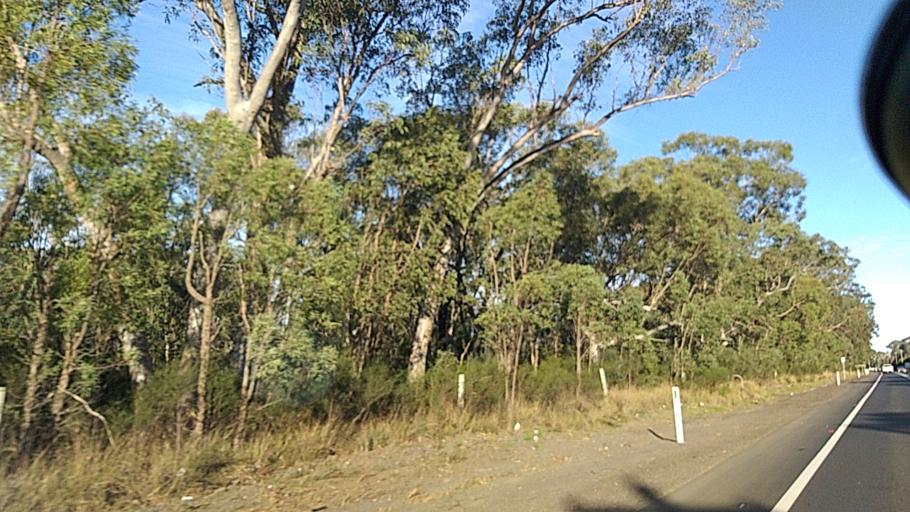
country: AU
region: New South Wales
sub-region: Hawkesbury
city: South Windsor
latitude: -33.6533
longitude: 150.7934
